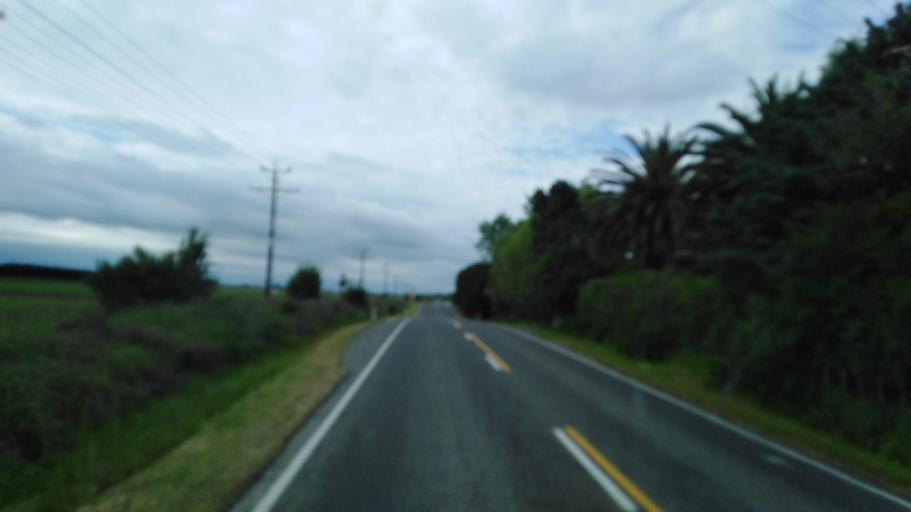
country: NZ
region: Manawatu-Wanganui
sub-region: Rangitikei District
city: Bulls
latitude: -40.1223
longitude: 175.3552
